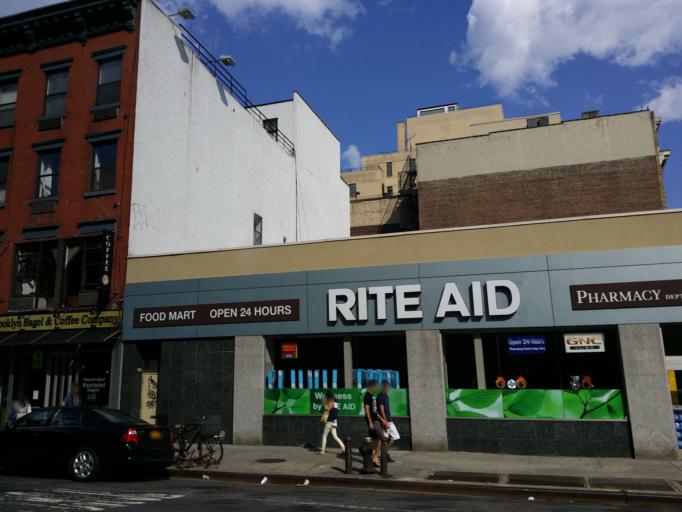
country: US
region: New Jersey
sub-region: Hudson County
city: Weehawken
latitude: 40.7460
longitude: -73.9979
